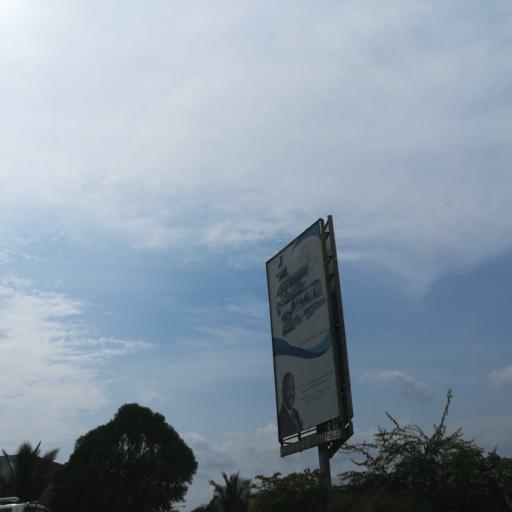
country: NG
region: Rivers
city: Port Harcourt
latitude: 4.8438
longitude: 7.0148
